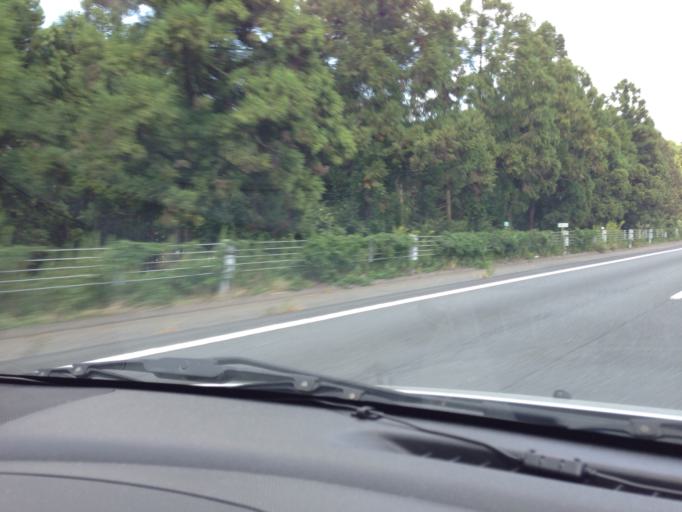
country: JP
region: Ibaraki
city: Ishioka
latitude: 36.2251
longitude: 140.2887
